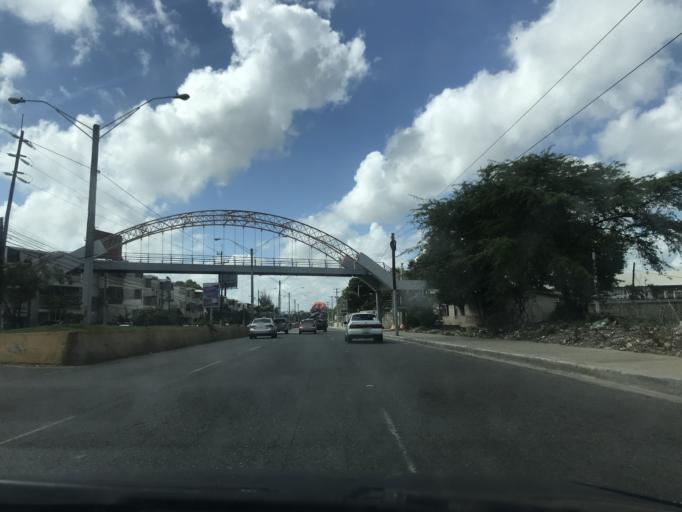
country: DO
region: Santiago
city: Santiago de los Caballeros
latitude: 19.4787
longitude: -70.7256
